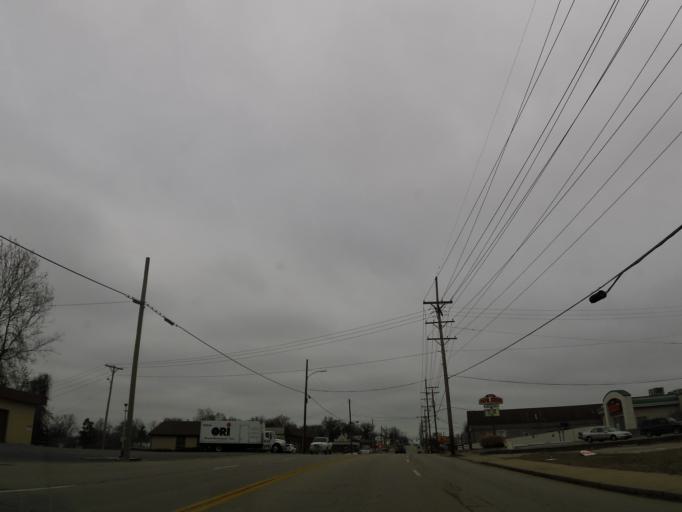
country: US
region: Kentucky
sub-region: Franklin County
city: Frankfort
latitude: 38.2018
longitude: -84.8519
